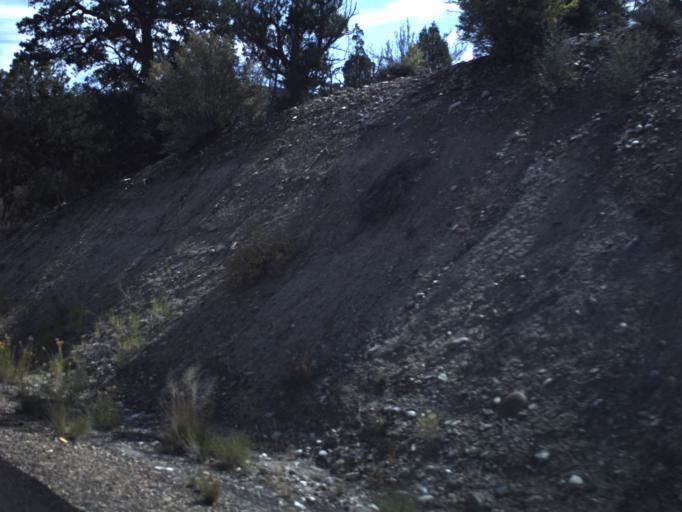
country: US
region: Utah
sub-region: Garfield County
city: Panguitch
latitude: 37.6213
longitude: -111.8696
